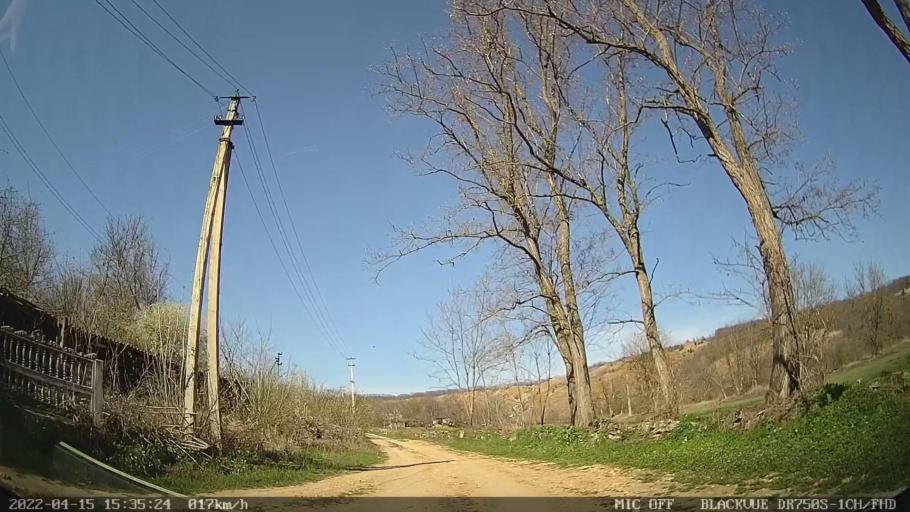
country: MD
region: Raionul Ocnita
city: Otaci
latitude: 48.3454
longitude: 27.9308
